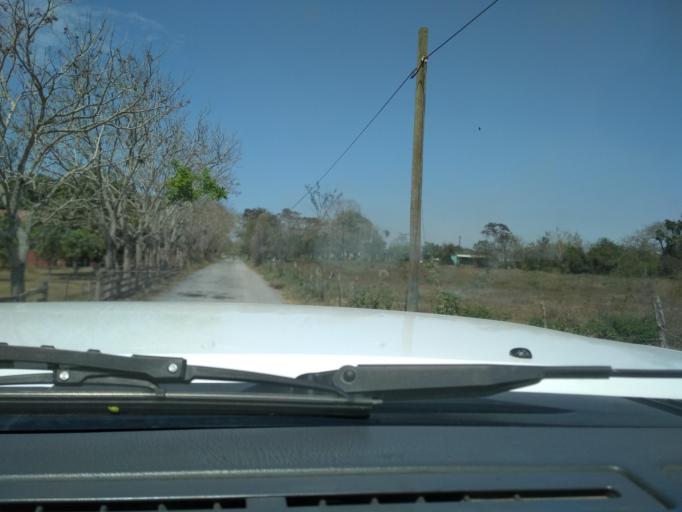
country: MX
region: Veracruz
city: Manlio Fabio Altamirano
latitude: 19.1536
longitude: -96.3318
